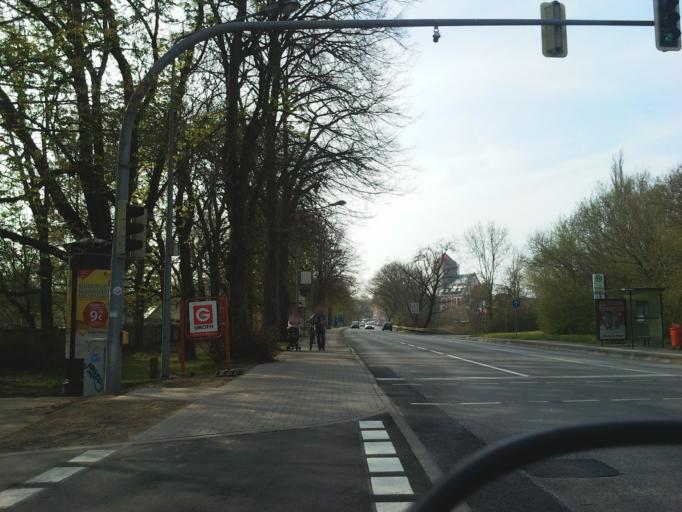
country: DE
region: Mecklenburg-Vorpommern
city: Rostock
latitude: 54.0835
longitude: 12.1534
